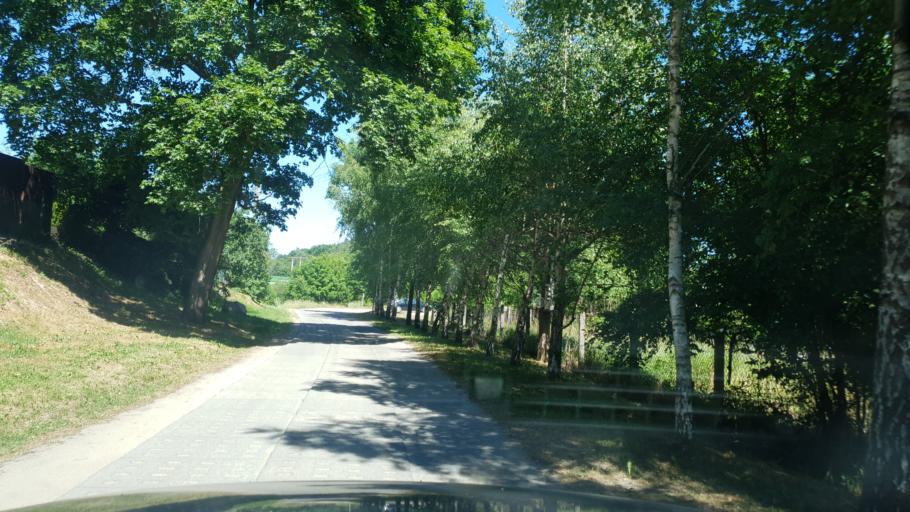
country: PL
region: Pomeranian Voivodeship
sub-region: Gdynia
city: Wielki Kack
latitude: 54.4578
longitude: 18.4849
